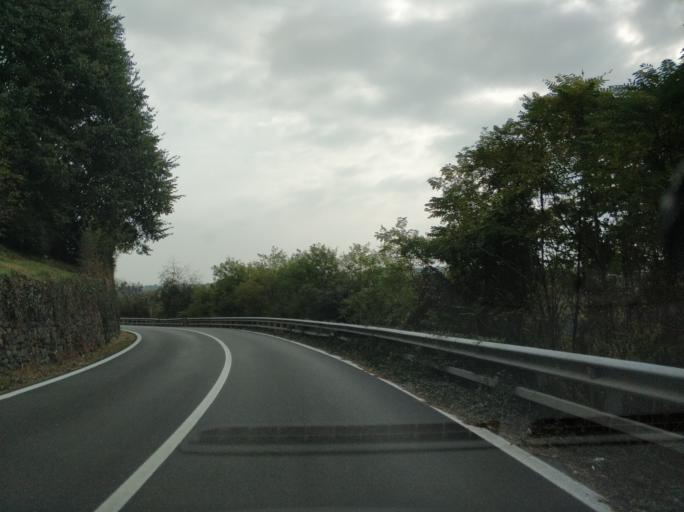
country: IT
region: Piedmont
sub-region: Provincia di Torino
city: Baldissero Canavese
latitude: 45.4152
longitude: 7.7561
